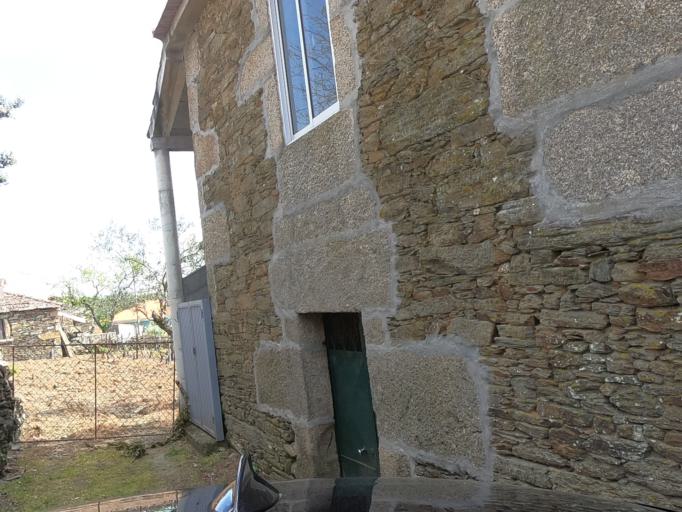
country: PT
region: Vila Real
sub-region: Vila Real
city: Vila Real
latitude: 41.2653
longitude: -7.6856
